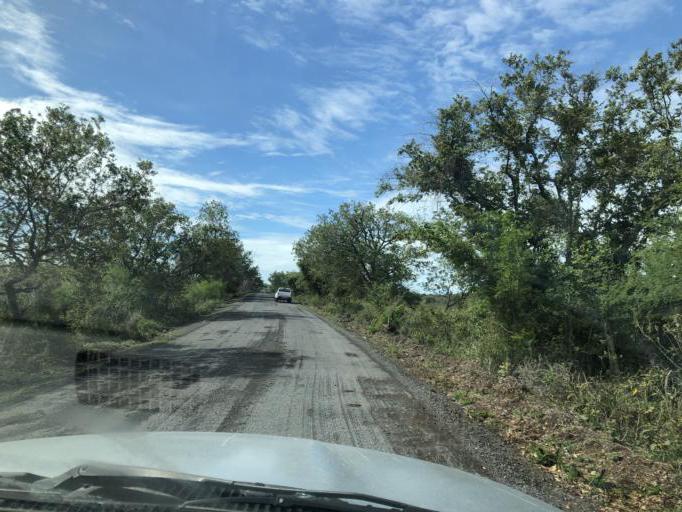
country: MX
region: Veracruz
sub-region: Alto Lucero de Gutierrez Barrios
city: Palma Sola
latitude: 19.7908
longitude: -96.5528
